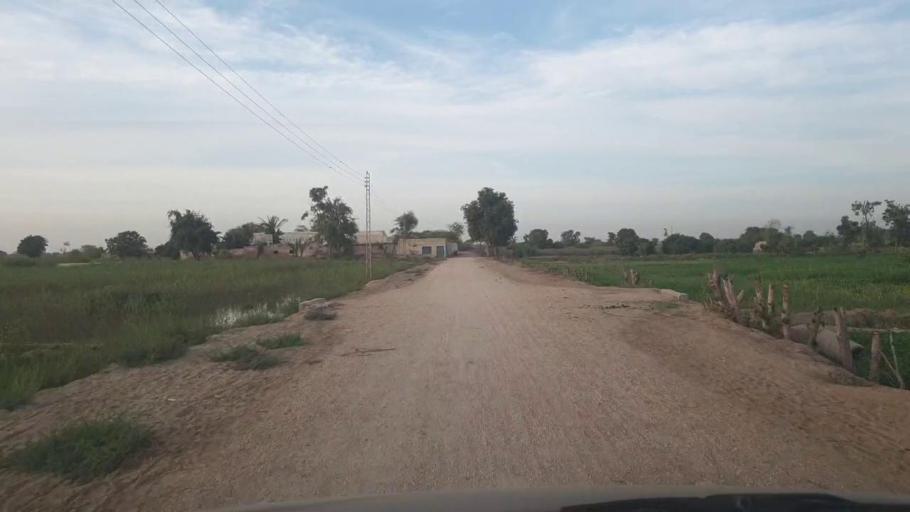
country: PK
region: Sindh
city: Kunri
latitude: 25.2404
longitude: 69.5593
